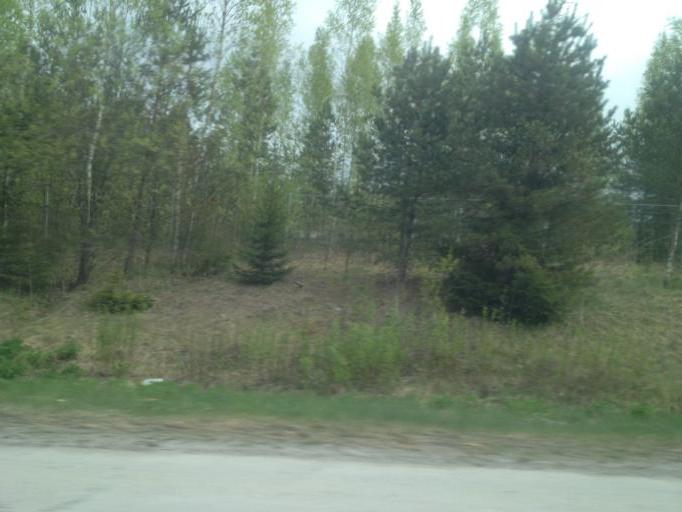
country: FI
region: Uusimaa
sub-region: Helsinki
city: Hyvinge
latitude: 60.5952
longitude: 24.7980
